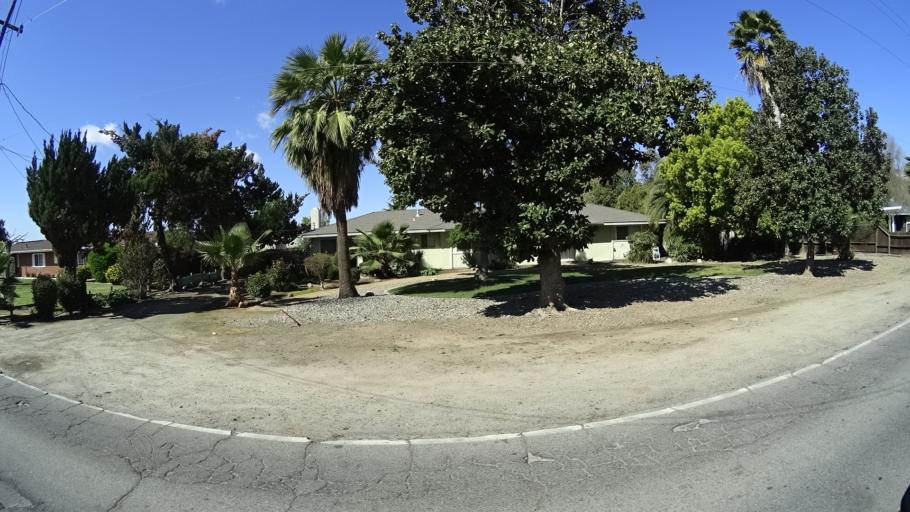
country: US
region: California
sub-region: Fresno County
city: West Park
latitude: 36.7921
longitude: -119.8894
